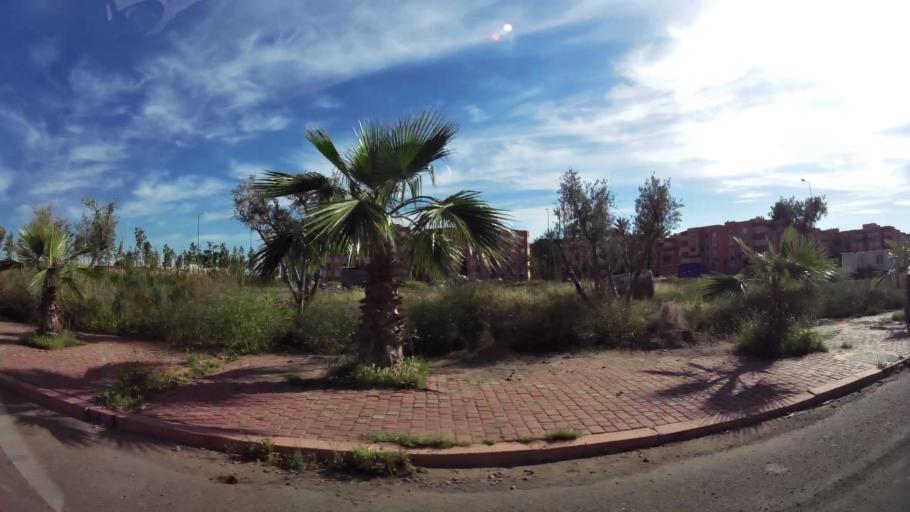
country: MA
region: Marrakech-Tensift-Al Haouz
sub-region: Marrakech
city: Marrakesh
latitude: 31.6737
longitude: -8.0526
